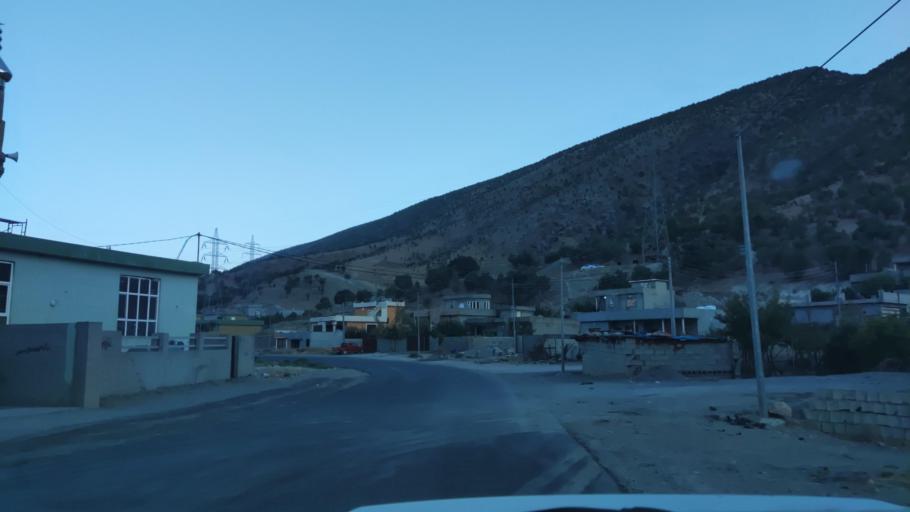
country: IQ
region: Arbil
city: Ruwandiz
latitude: 36.5920
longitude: 44.3858
